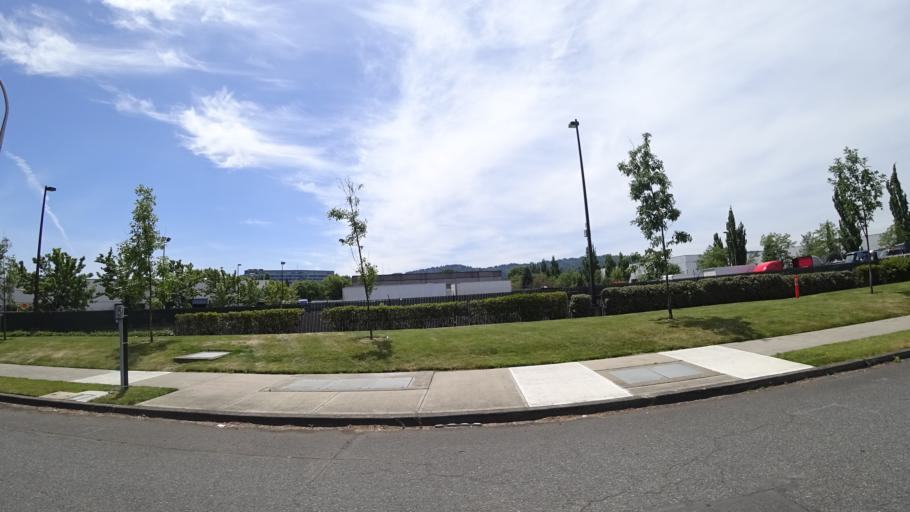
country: US
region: Oregon
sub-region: Multnomah County
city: Portland
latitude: 45.5590
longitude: -122.7005
